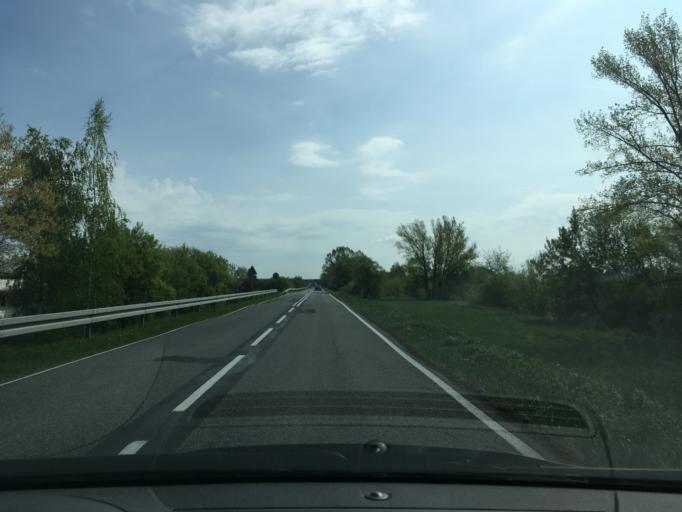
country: PL
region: Lublin Voivodeship
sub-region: Powiat rycki
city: Deblin
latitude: 51.4762
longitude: 21.8889
